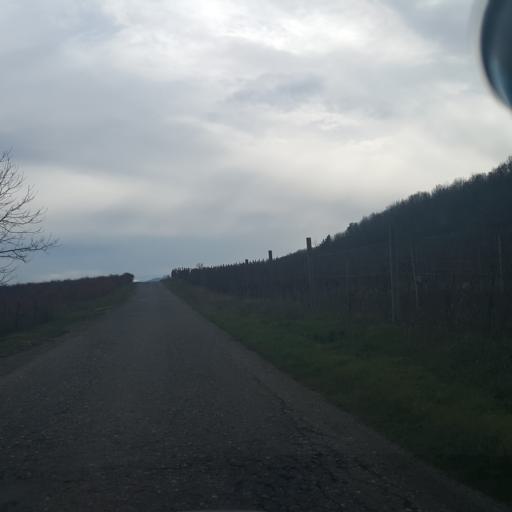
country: RS
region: Central Serbia
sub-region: Zajecarski Okrug
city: Knjazevac
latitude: 43.6171
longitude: 22.2610
